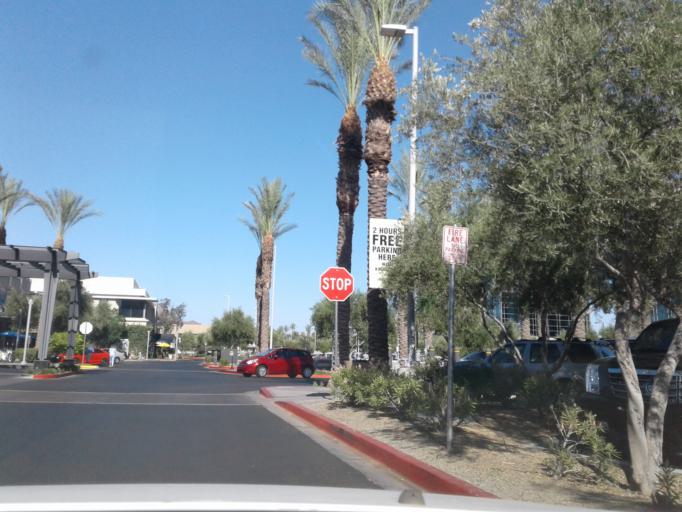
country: US
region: Arizona
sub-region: Maricopa County
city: Phoenix
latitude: 33.5101
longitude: -112.0286
